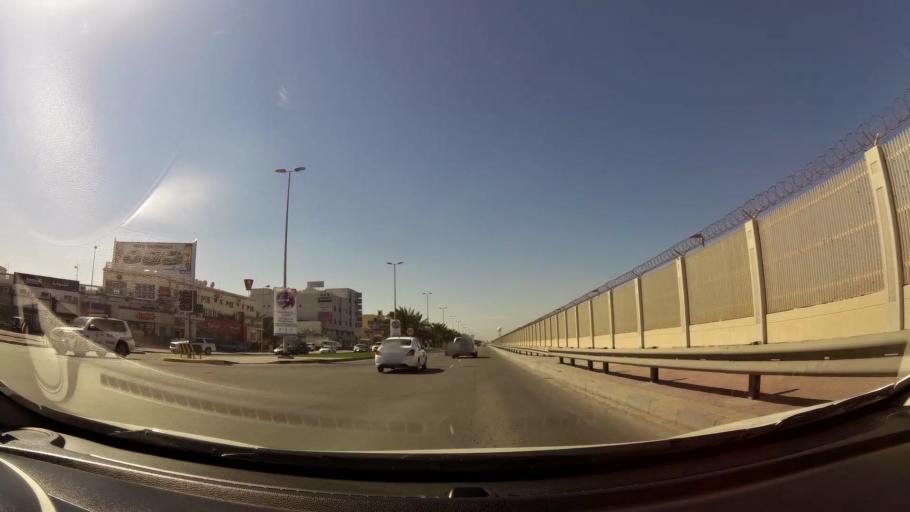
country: BH
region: Muharraq
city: Al Hadd
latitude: 26.2574
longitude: 50.6492
